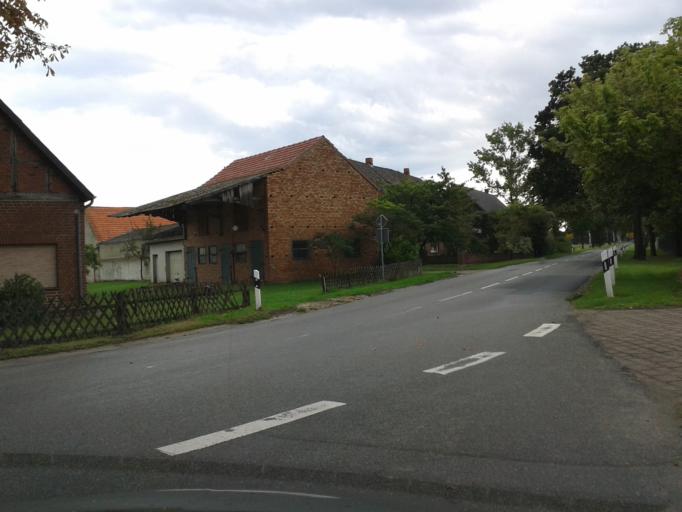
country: DE
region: Lower Saxony
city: Woltersdorf
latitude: 52.9518
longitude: 11.2234
